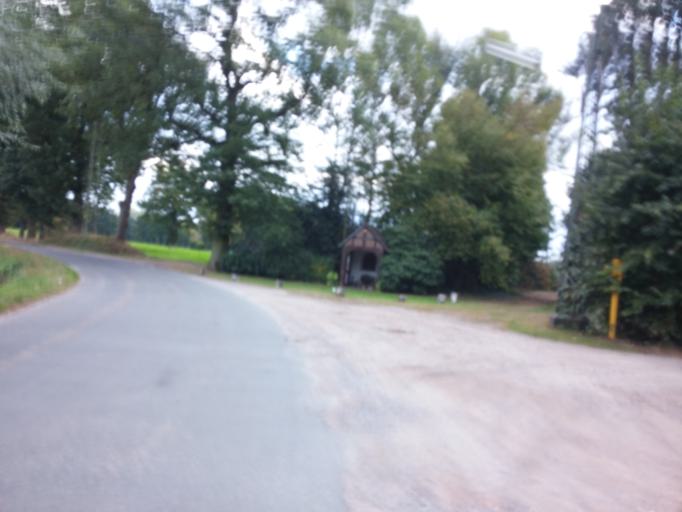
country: DE
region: North Rhine-Westphalia
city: Dorsten
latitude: 51.6432
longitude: 6.9741
